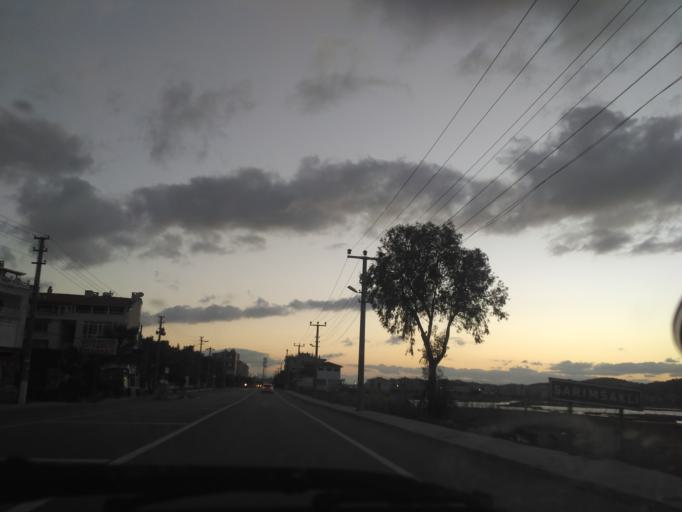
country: TR
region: Balikesir
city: Ayvalik
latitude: 39.2778
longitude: 26.6705
